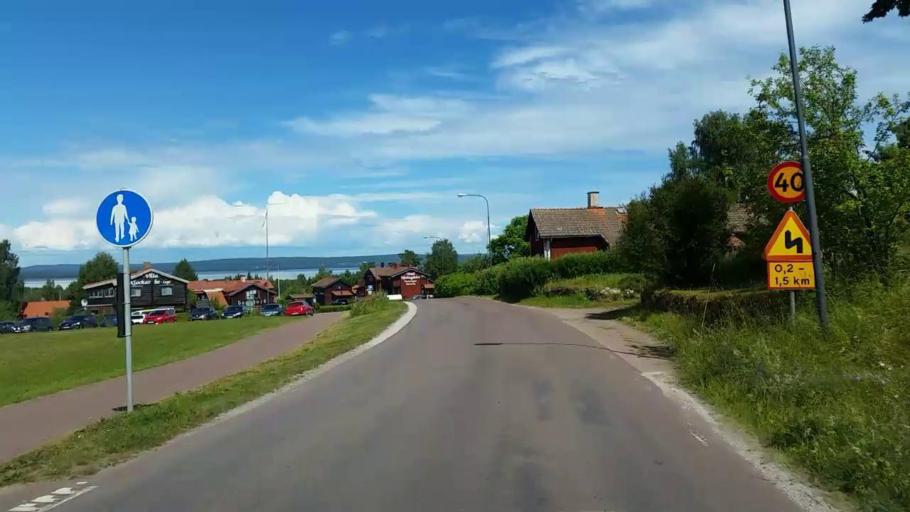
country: SE
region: Dalarna
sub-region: Leksand Municipality
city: Leksand
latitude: 60.8239
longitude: 14.9926
